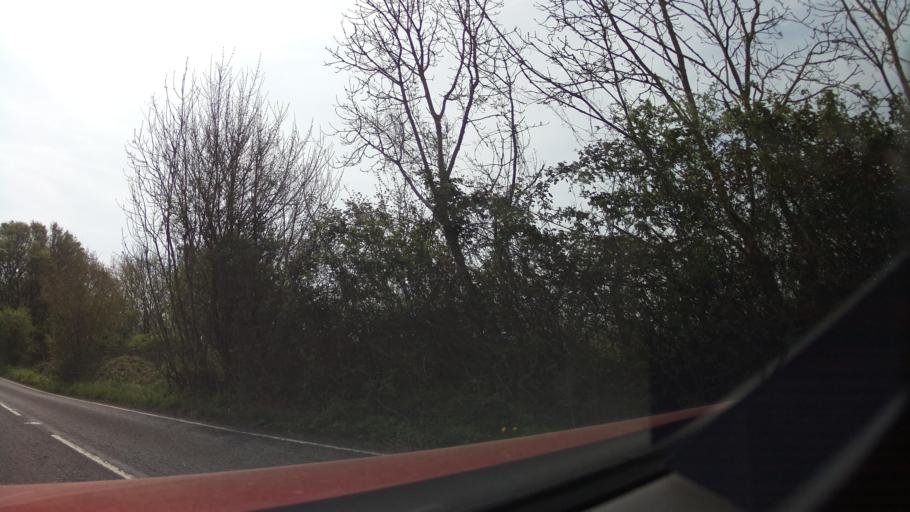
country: GB
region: England
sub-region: Somerset
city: Street
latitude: 51.1115
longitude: -2.7613
